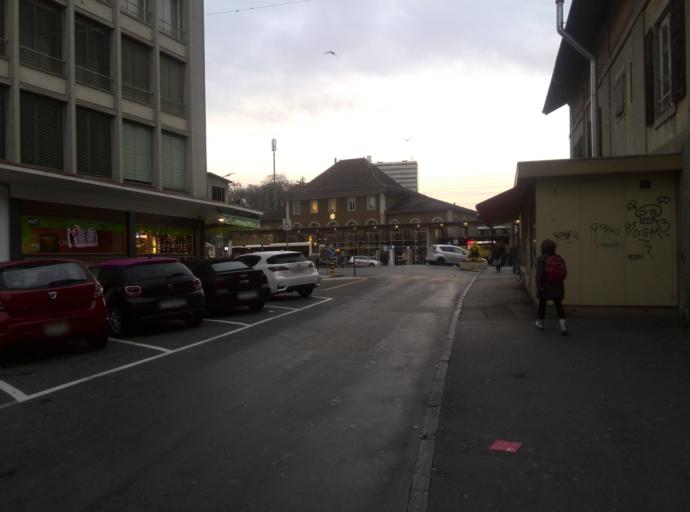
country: CH
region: Vaud
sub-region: Morges District
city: Morges
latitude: 46.5108
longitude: 6.4952
